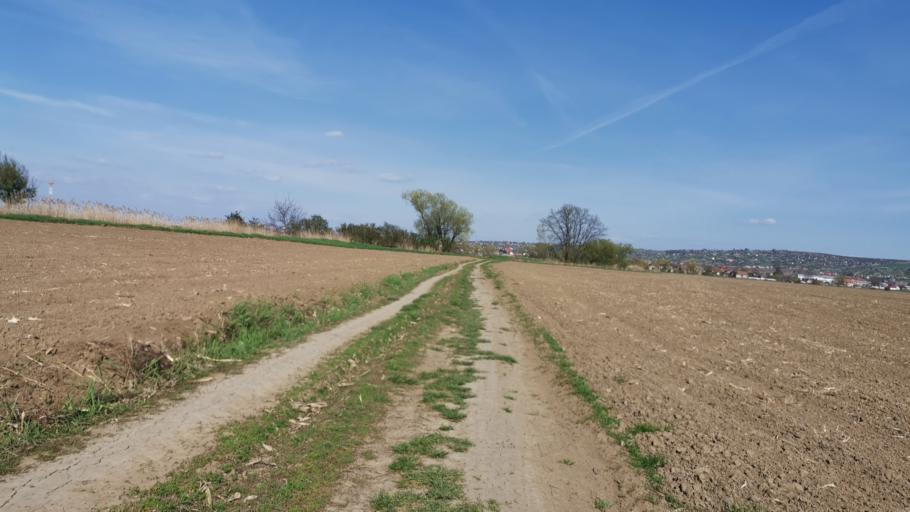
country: SK
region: Trnavsky
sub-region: Okres Skalica
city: Holic
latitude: 48.8189
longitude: 17.1759
